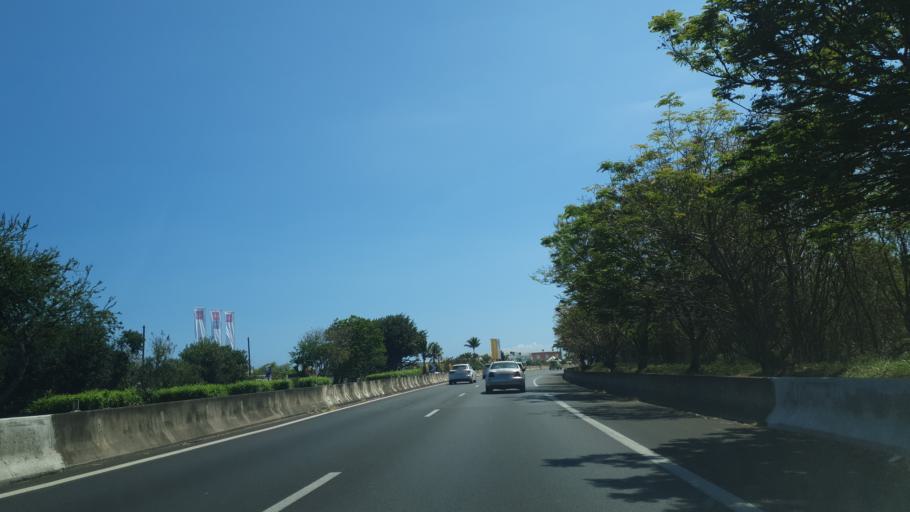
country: RE
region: Reunion
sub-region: Reunion
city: Saint-Pierre
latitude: -21.3327
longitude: 55.4628
